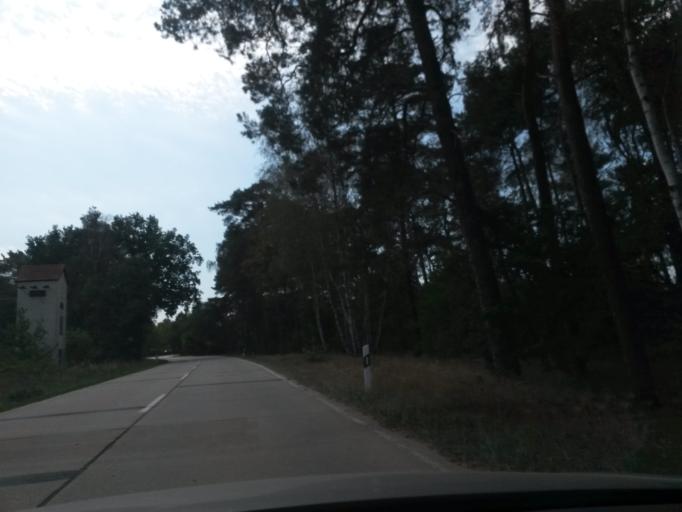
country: DE
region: Saxony-Anhalt
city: Jerichow
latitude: 52.4715
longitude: 12.0238
